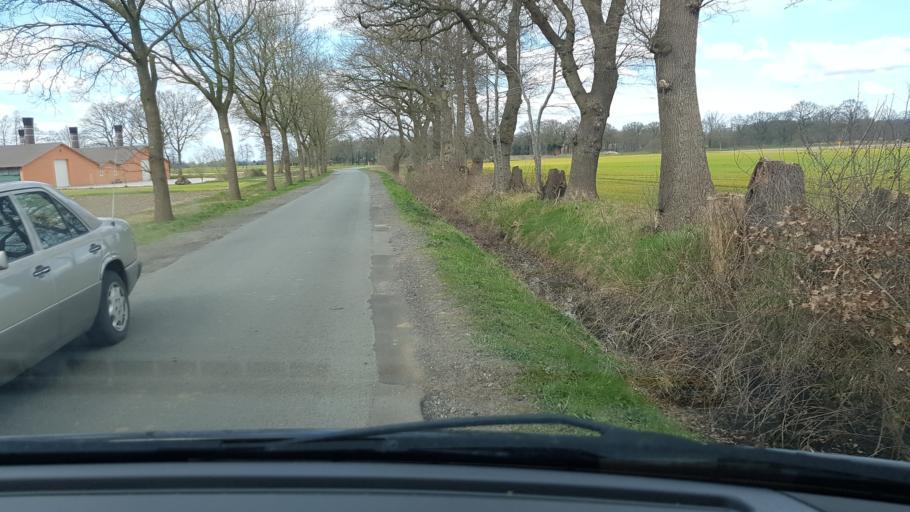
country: DE
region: Lower Saxony
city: Edewecht
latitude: 53.1084
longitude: 7.9434
